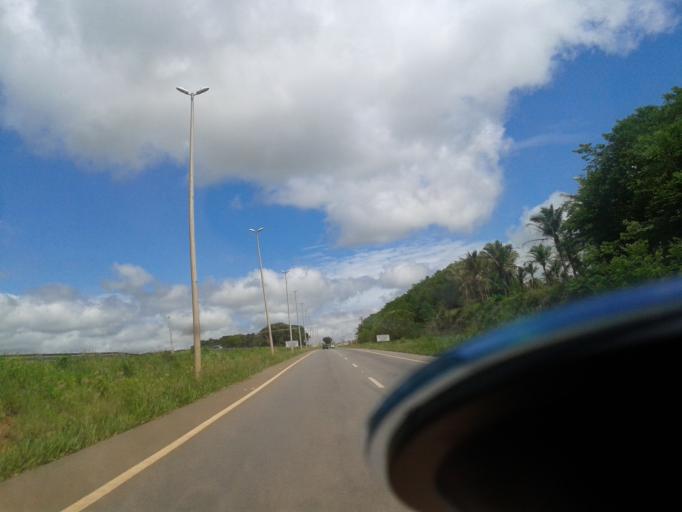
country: BR
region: Goias
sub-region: Goianira
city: Goianira
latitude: -16.4764
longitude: -49.4335
